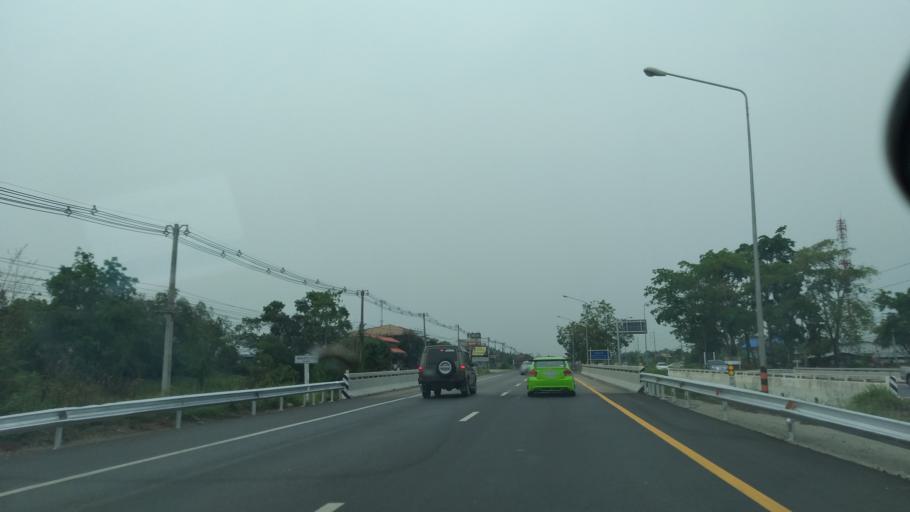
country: TH
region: Chon Buri
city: Ko Chan
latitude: 13.3752
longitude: 101.2762
